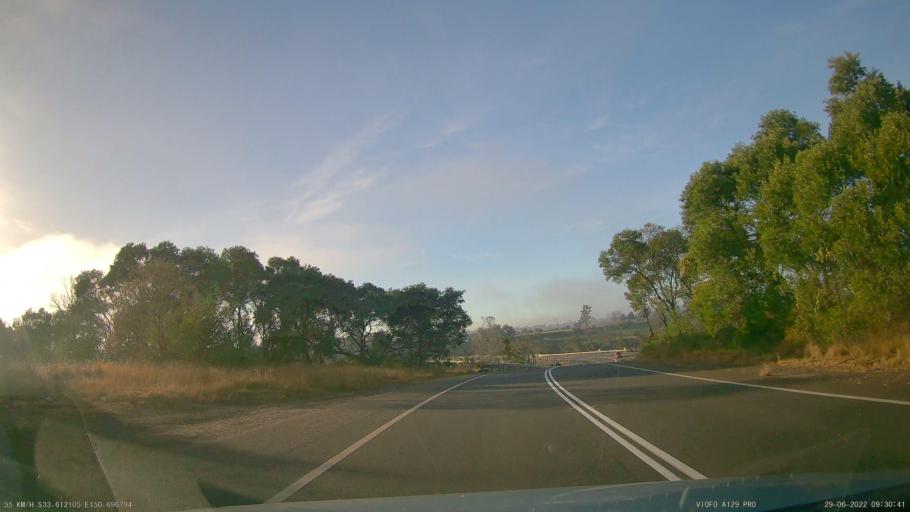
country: AU
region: New South Wales
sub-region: Hawkesbury
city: Richmond
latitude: -33.6123
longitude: 150.6971
